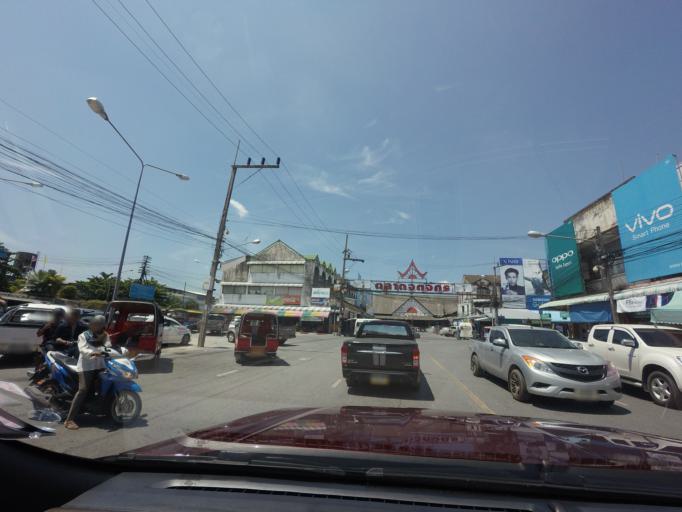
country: TH
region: Yala
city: Yala
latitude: 6.5596
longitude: 101.2931
